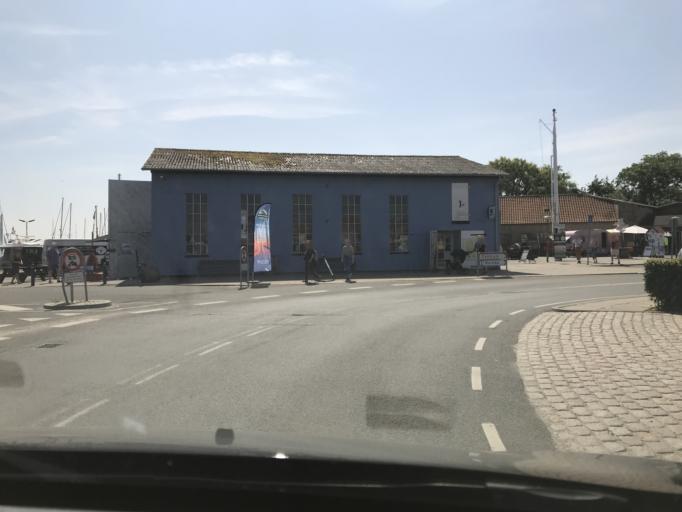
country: DK
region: South Denmark
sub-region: AEro Kommune
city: AEroskobing
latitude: 54.8915
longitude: 10.4121
